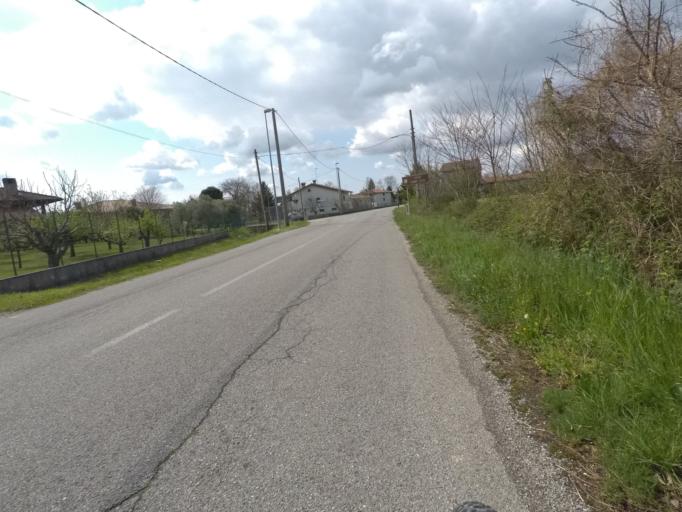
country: IT
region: Friuli Venezia Giulia
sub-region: Provincia di Udine
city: Gemona
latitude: 46.2590
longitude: 13.1239
